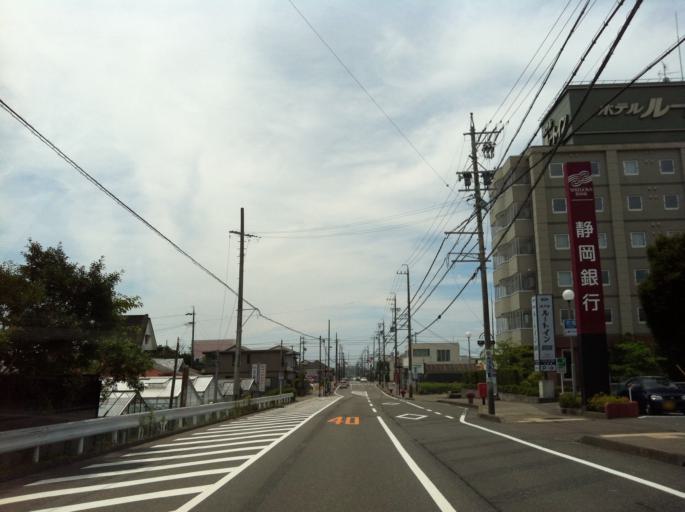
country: JP
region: Shizuoka
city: Sagara
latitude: 34.6465
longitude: 138.1283
